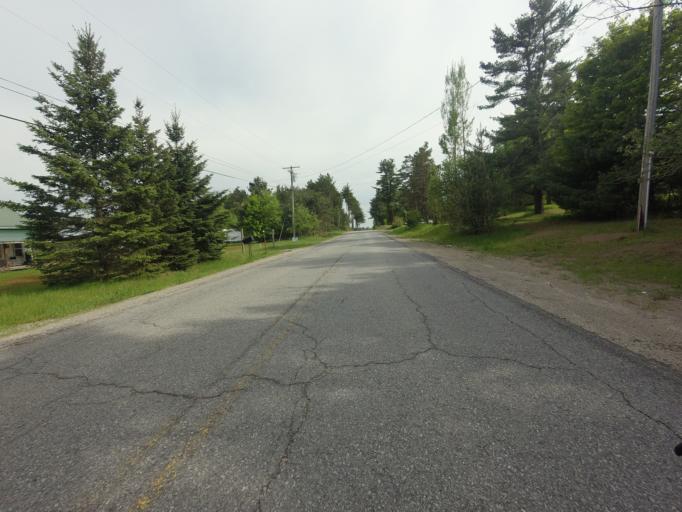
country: US
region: New York
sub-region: St. Lawrence County
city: Gouverneur
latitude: 44.2777
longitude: -75.2054
